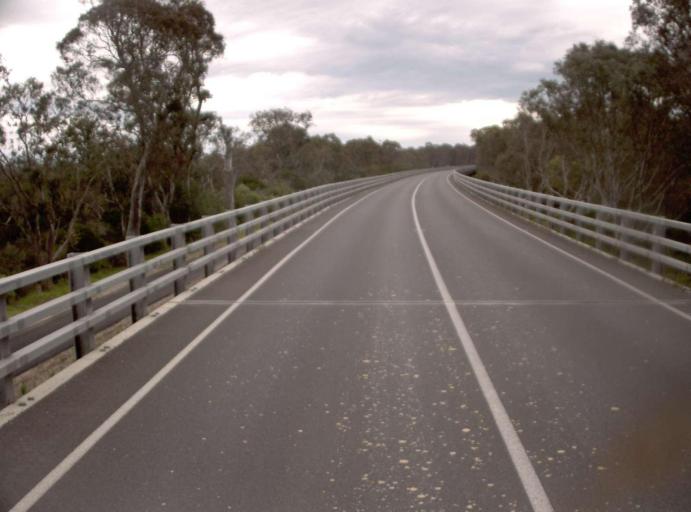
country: AU
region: Victoria
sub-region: Wellington
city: Sale
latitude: -38.1382
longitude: 147.0784
